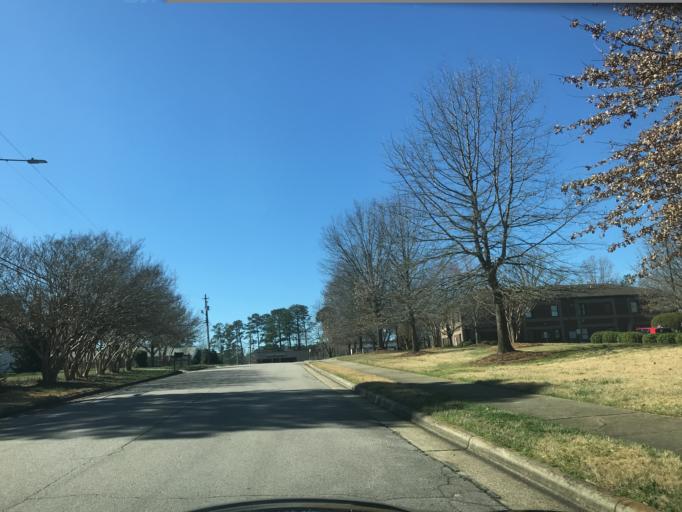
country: US
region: North Carolina
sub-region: Wake County
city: West Raleigh
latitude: 35.8532
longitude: -78.6409
